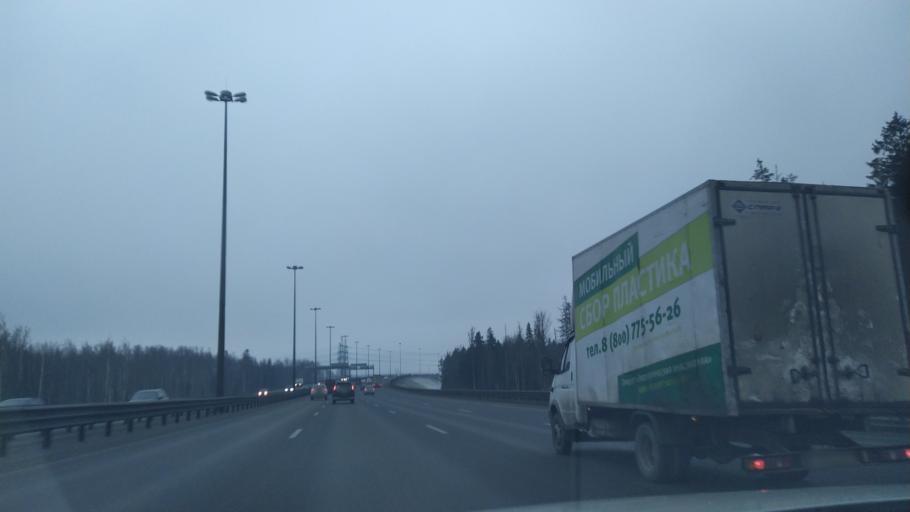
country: RU
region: St.-Petersburg
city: Krasnogvargeisky
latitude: 59.9372
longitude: 30.5385
